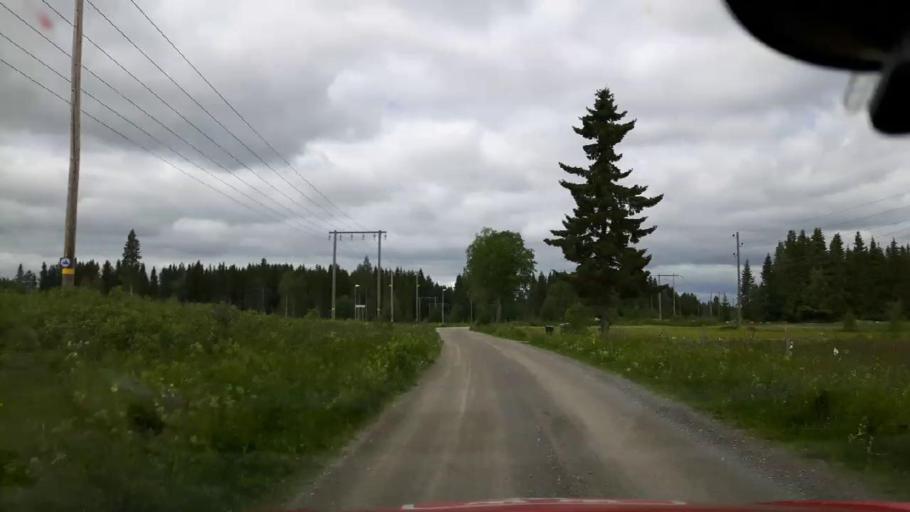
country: SE
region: Jaemtland
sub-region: OEstersunds Kommun
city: Brunflo
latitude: 63.0963
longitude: 14.8166
